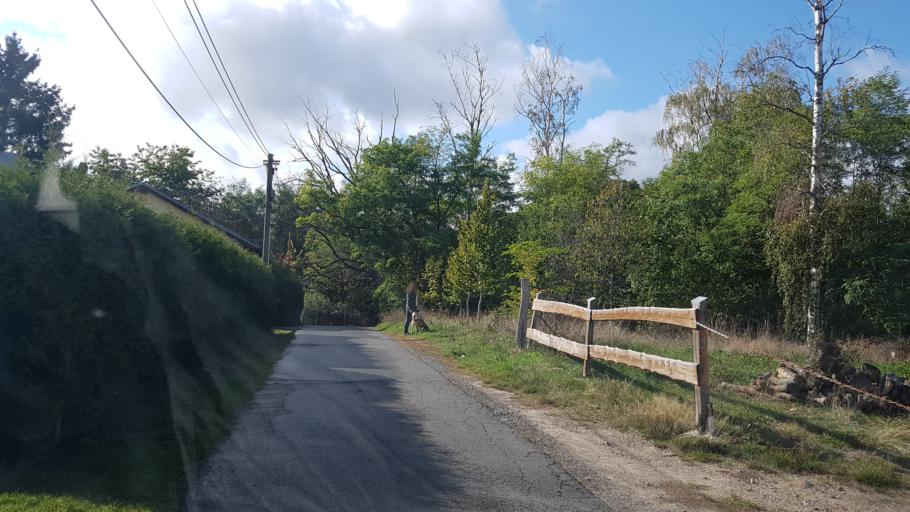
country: DE
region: Saxony
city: Dahlen
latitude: 51.3730
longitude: 13.0019
